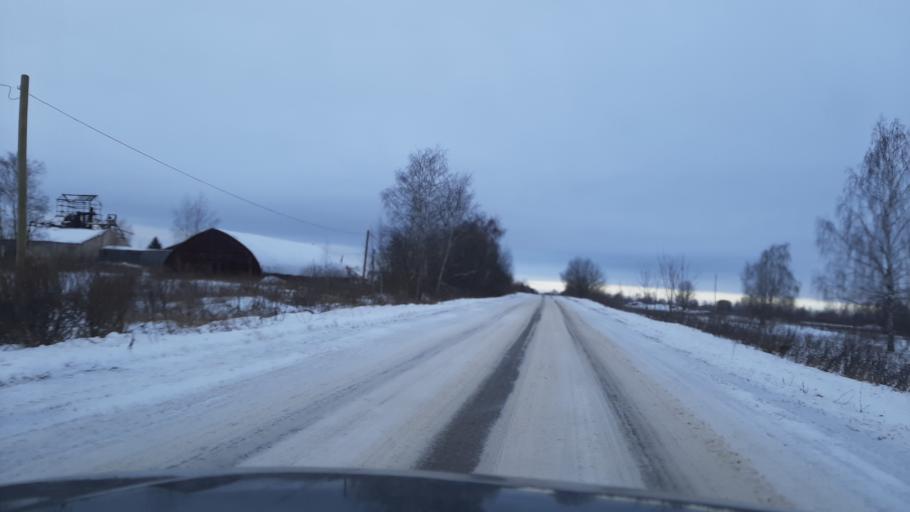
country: RU
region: Kostroma
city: Volgorechensk
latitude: 57.4348
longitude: 41.0653
